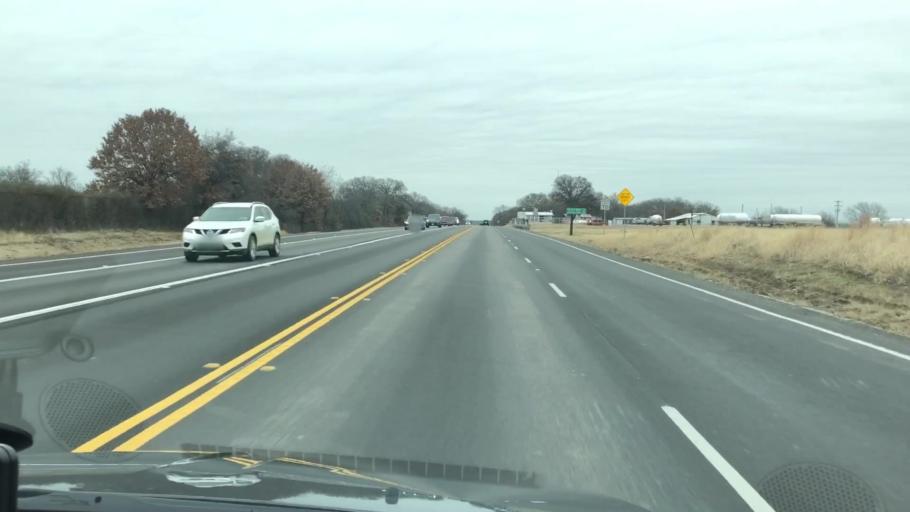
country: US
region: Texas
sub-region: Palo Pinto County
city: Mineral Wells
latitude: 32.5260
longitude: -98.1260
